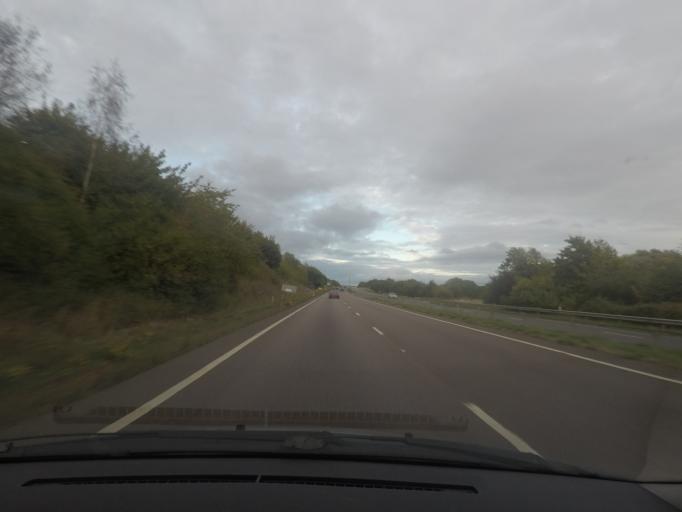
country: GB
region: England
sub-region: Northamptonshire
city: Brackley
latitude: 52.0590
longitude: -1.1022
